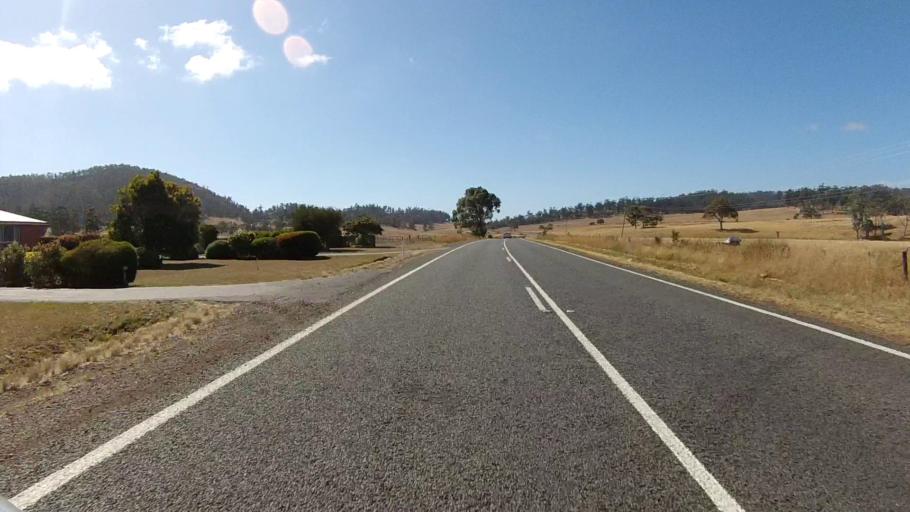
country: AU
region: Tasmania
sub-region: Sorell
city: Sorell
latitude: -42.4405
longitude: 147.9281
